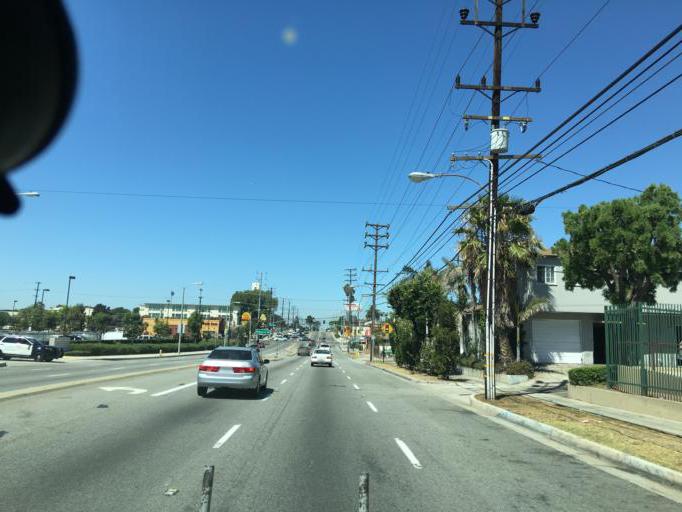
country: US
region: California
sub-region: Los Angeles County
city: West Athens
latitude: 33.9310
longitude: -118.2981
